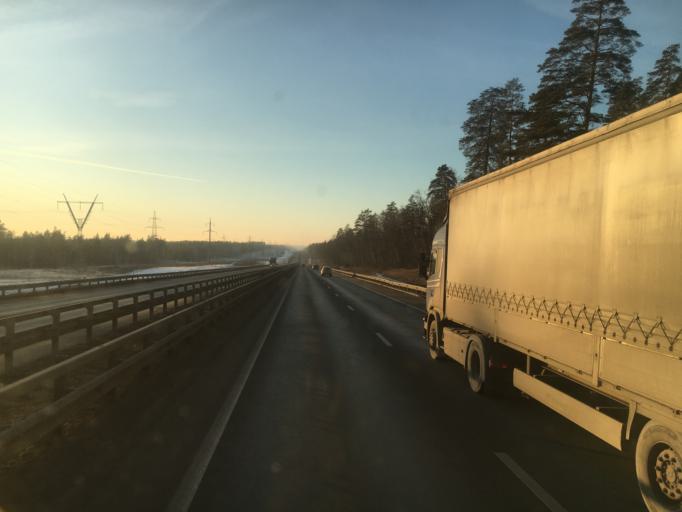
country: RU
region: Samara
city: Povolzhskiy
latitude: 53.5178
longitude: 49.7823
